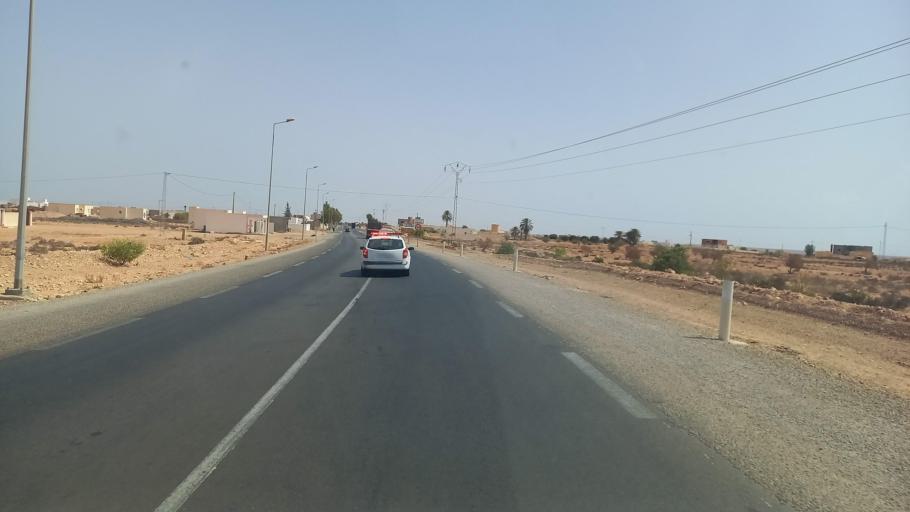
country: TN
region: Madanin
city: Medenine
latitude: 33.3712
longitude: 10.6901
